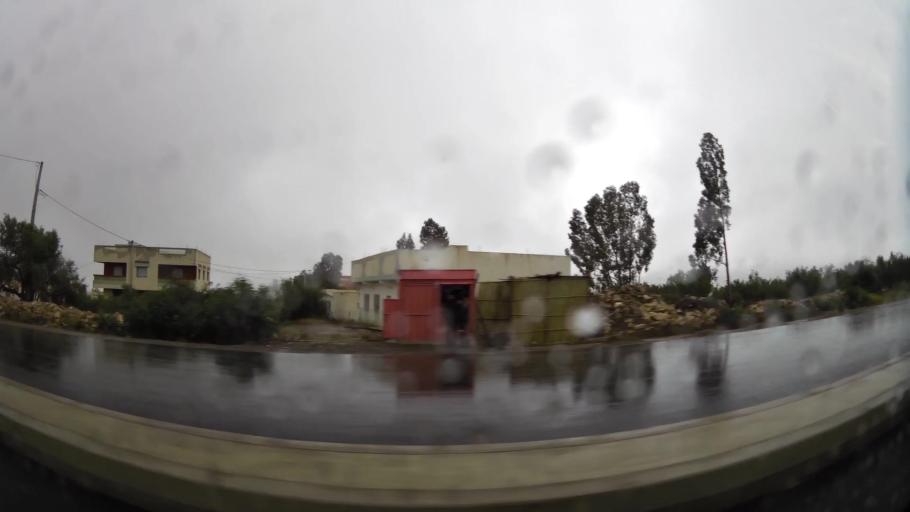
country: MA
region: Oriental
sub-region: Nador
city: Midar
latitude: 34.8485
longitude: -3.7217
